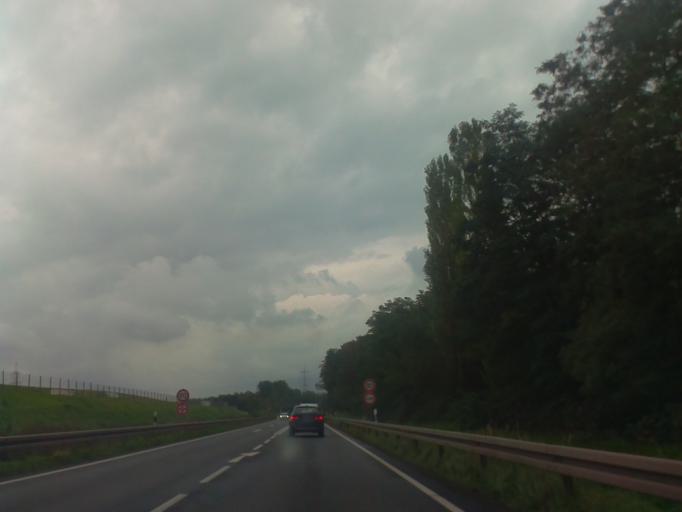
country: DE
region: Bavaria
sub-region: Regierungsbezirk Unterfranken
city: Kleinostheim
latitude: 50.0005
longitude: 9.0437
